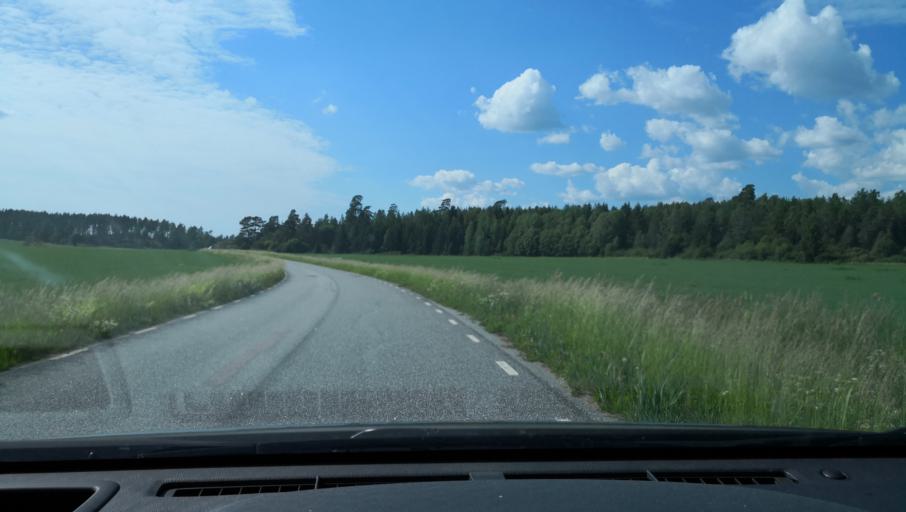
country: SE
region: Uppsala
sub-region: Enkopings Kommun
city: Orsundsbro
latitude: 59.8386
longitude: 17.2970
